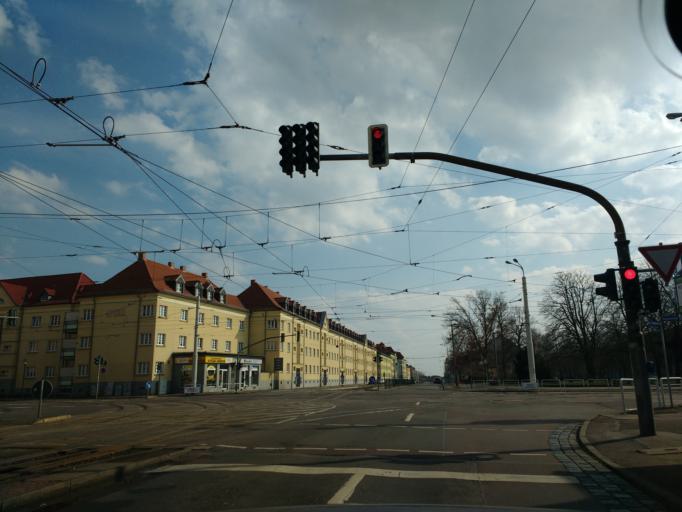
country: DE
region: Saxony-Anhalt
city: Halle (Saale)
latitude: 51.4570
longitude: 11.9719
